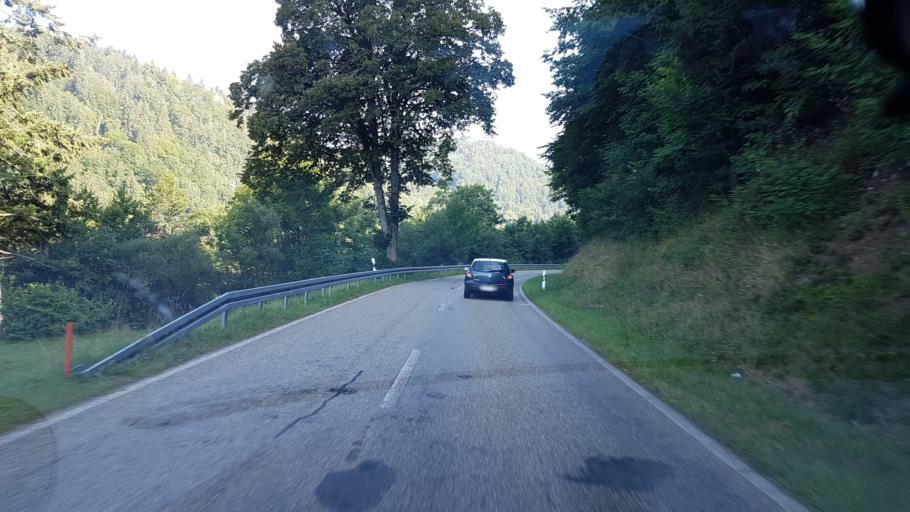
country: DE
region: Baden-Wuerttemberg
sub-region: Freiburg Region
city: Dachsberg
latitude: 47.7026
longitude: 8.1248
